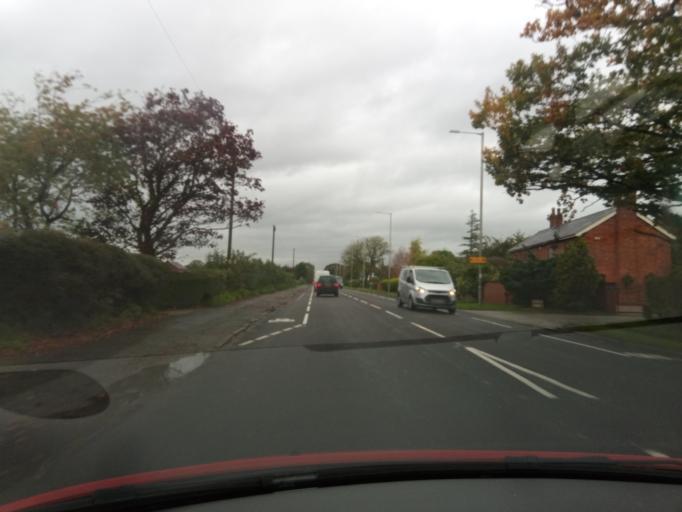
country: GB
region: England
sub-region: Lancashire
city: Preston
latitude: 53.8237
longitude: -2.7354
